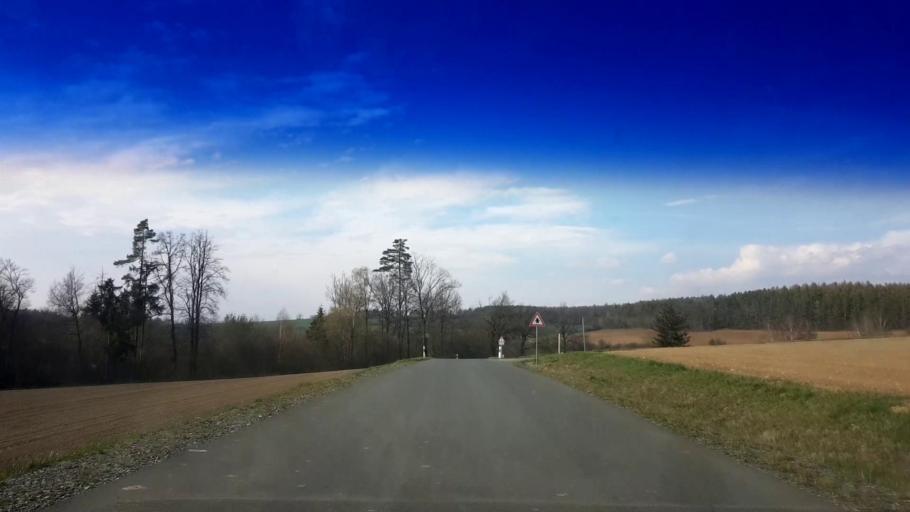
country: DE
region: Bavaria
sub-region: Upper Franconia
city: Harsdorf
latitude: 50.0301
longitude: 11.5887
